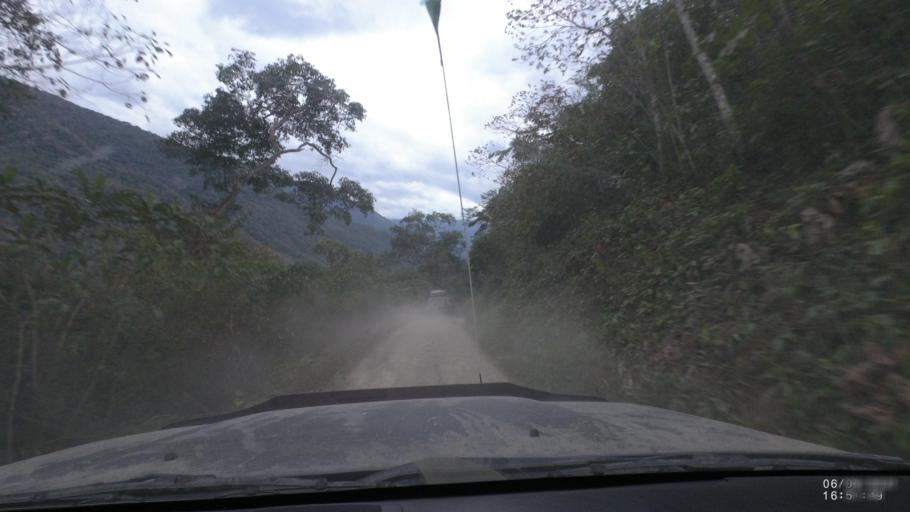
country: BO
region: La Paz
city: Quime
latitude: -16.4952
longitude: -66.7757
